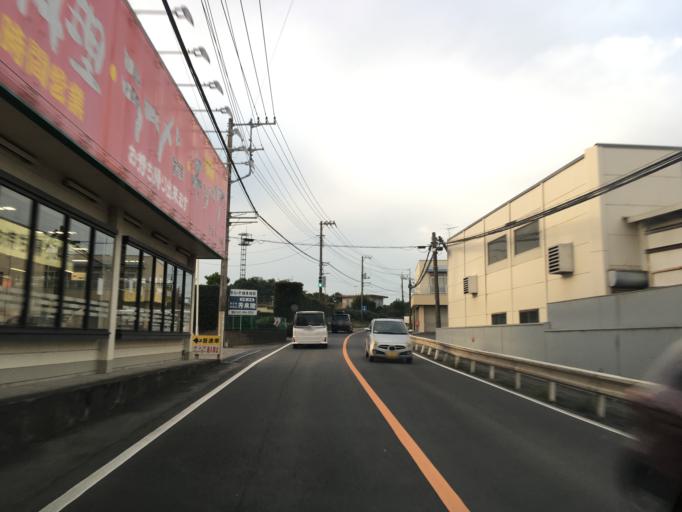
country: JP
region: Saitama
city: Sayama
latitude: 35.8818
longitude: 139.3776
